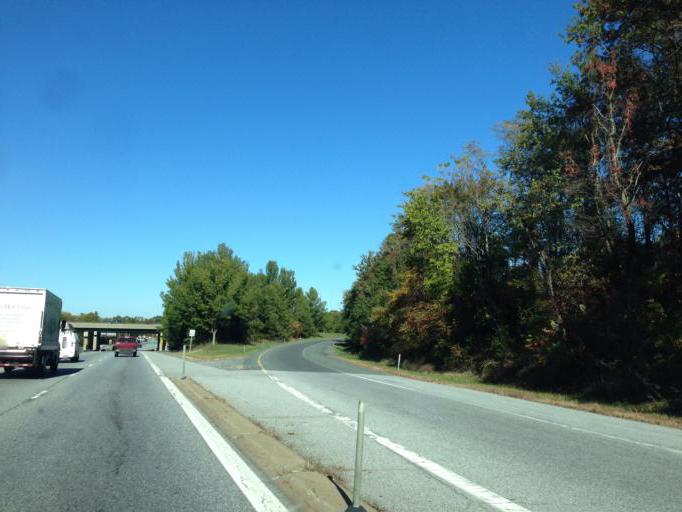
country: US
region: Maryland
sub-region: Carroll County
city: Mount Airy
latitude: 39.3575
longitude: -77.1676
